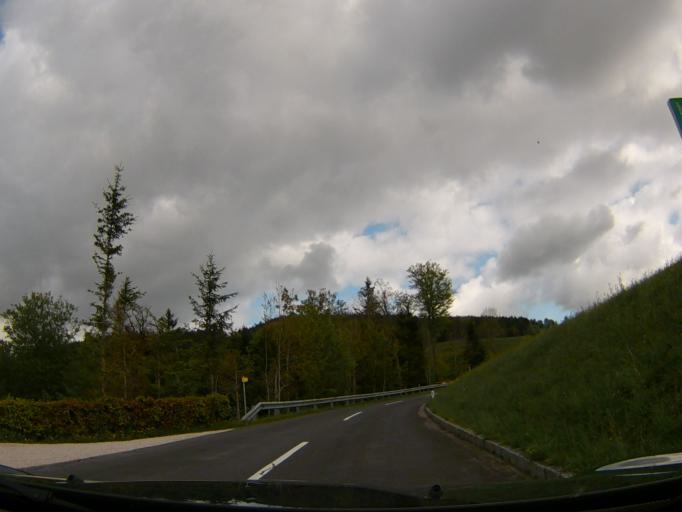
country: AT
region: Upper Austria
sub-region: Politischer Bezirk Vocklabruck
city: Tiefgraben
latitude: 47.8730
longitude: 13.3504
